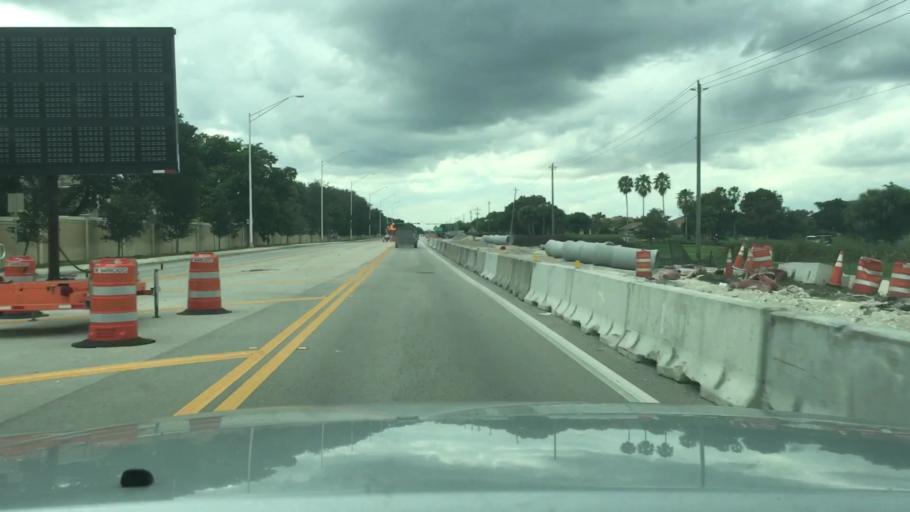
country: US
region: Florida
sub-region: Miami-Dade County
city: Country Club
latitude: 25.9932
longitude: -80.3479
